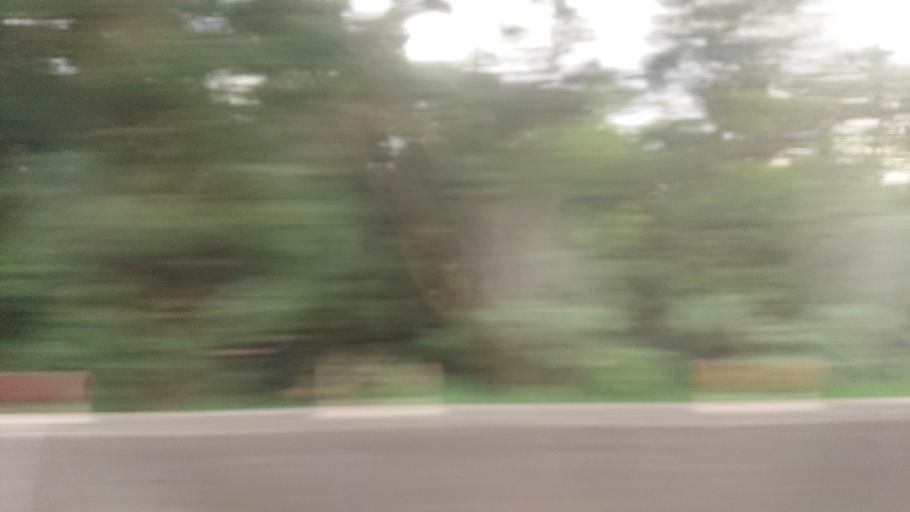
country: TW
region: Taiwan
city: Daxi
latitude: 24.8923
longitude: 121.2655
